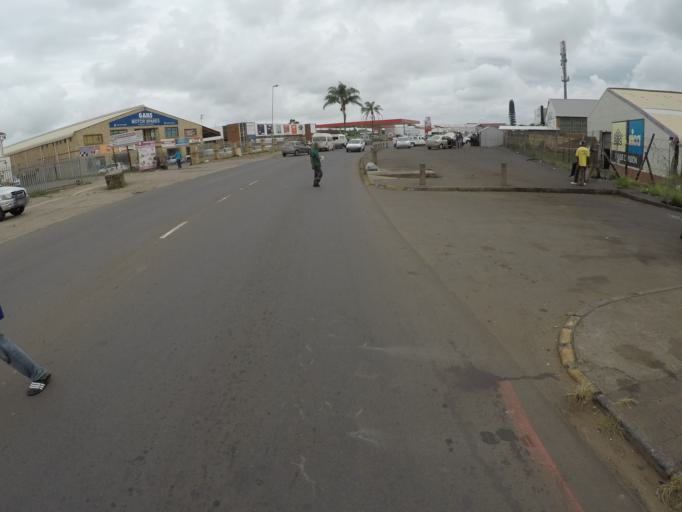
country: ZA
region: KwaZulu-Natal
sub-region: uThungulu District Municipality
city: Empangeni
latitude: -28.7697
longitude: 31.9057
